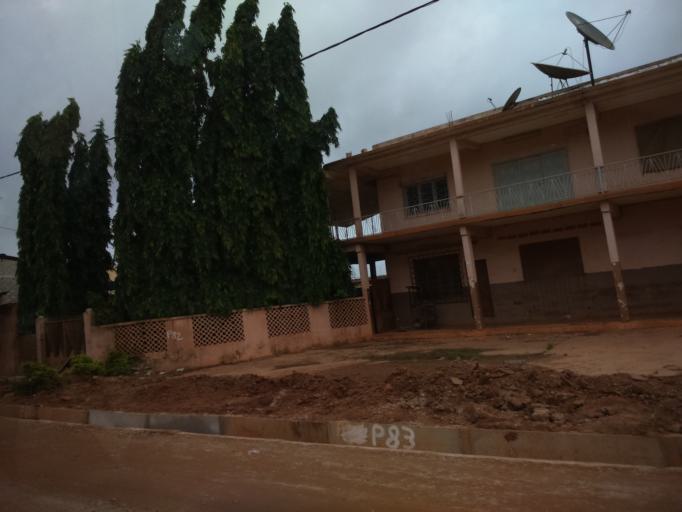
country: CI
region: Moyen-Comoe
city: Abengourou
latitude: 6.7261
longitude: -3.5009
